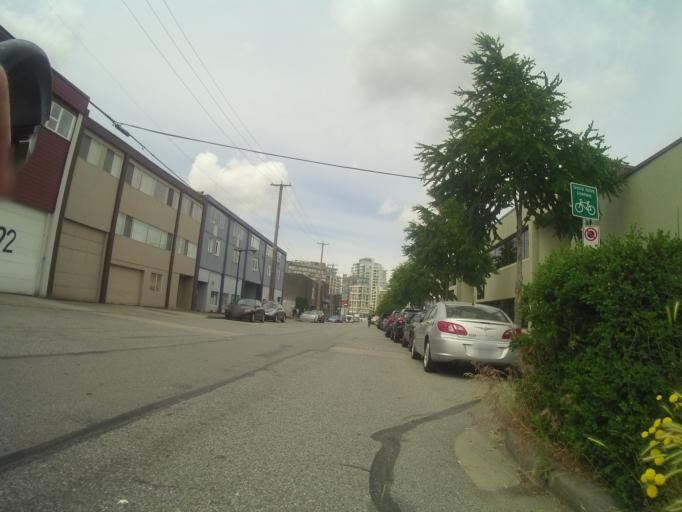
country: CA
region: British Columbia
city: Vancouver
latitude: 49.2685
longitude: -123.0975
